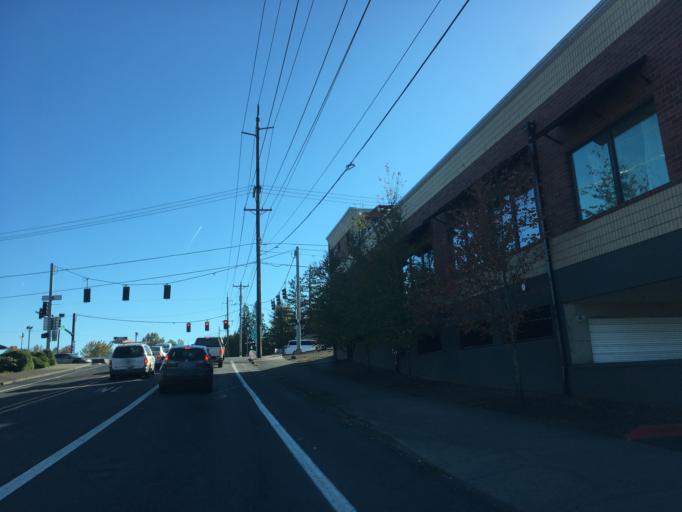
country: US
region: Oregon
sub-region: Multnomah County
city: Gresham
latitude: 45.4986
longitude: -122.4140
